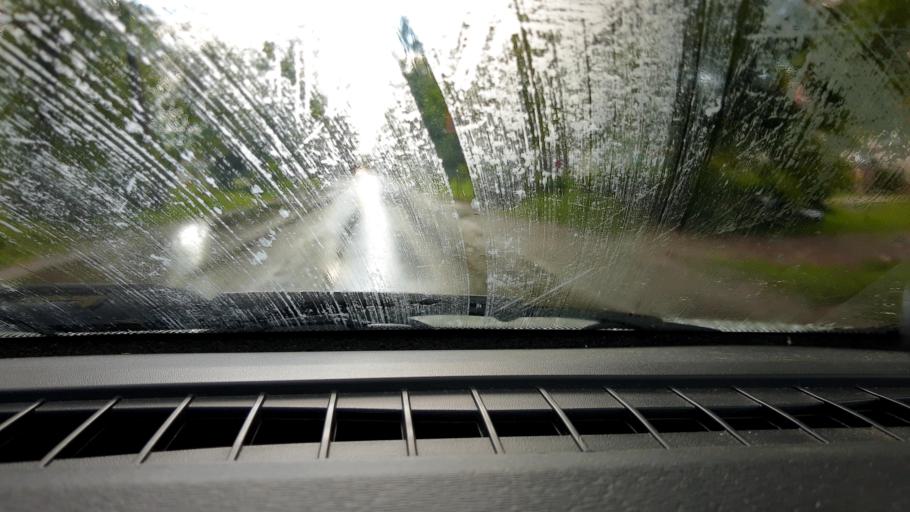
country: RU
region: Nizjnij Novgorod
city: Bogorodsk
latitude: 56.0968
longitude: 43.5083
